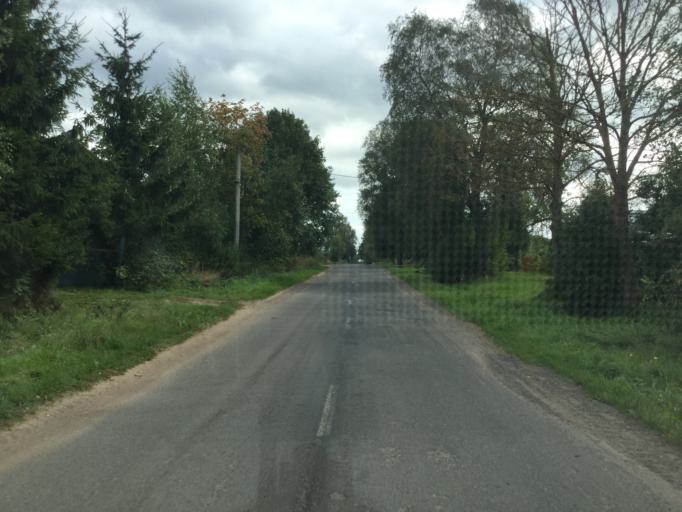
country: BY
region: Vitebsk
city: Vitebsk
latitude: 55.1469
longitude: 30.2815
